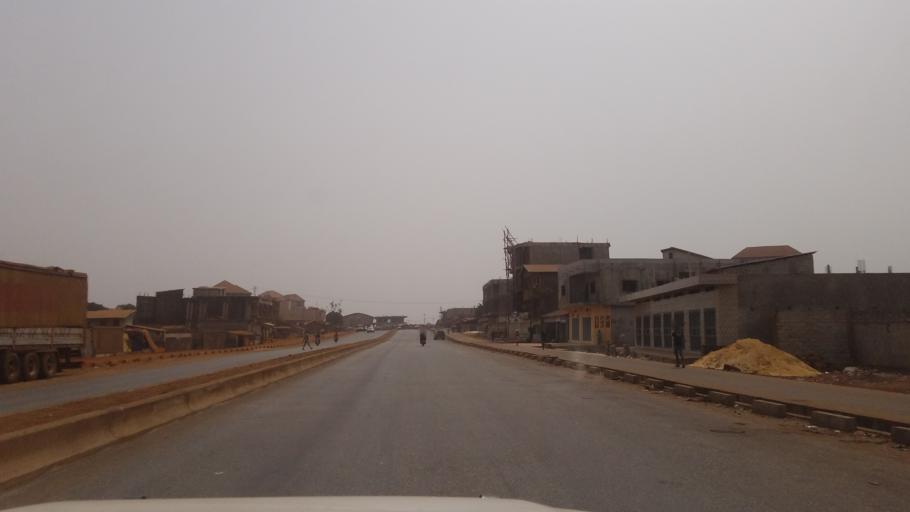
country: GN
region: Kindia
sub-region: Prefecture de Dubreka
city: Dubreka
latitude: 9.6823
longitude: -13.5284
